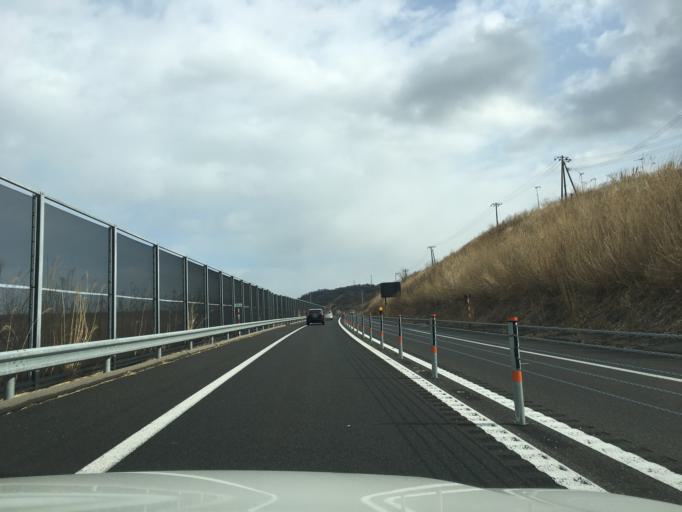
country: JP
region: Yamagata
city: Yuza
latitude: 39.3048
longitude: 139.9790
